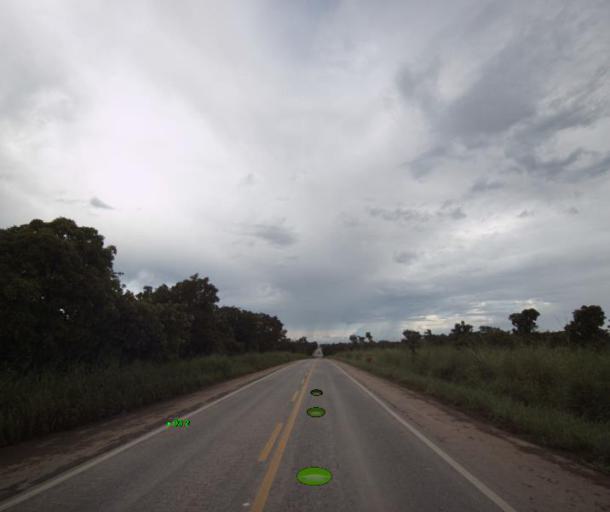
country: BR
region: Goias
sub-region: Porangatu
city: Porangatu
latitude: -13.5917
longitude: -49.0417
